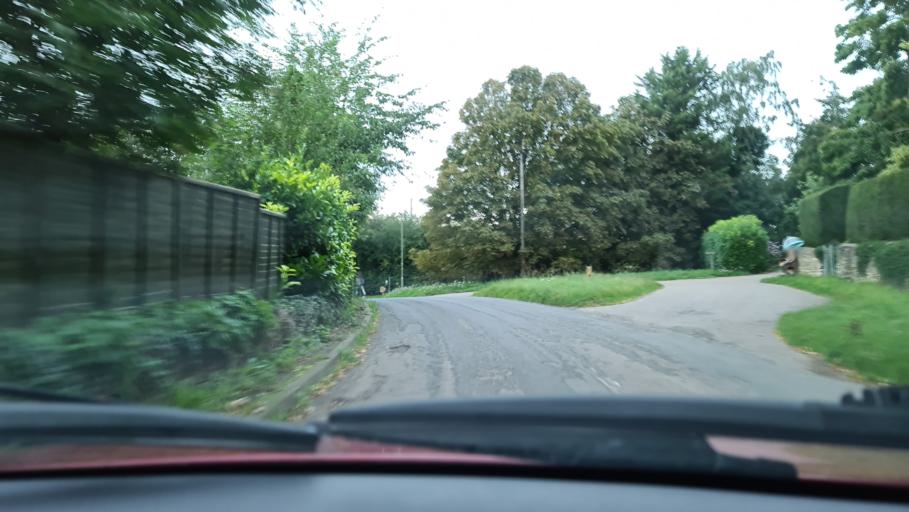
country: GB
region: England
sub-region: Oxfordshire
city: Somerton
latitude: 51.9560
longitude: -1.2772
